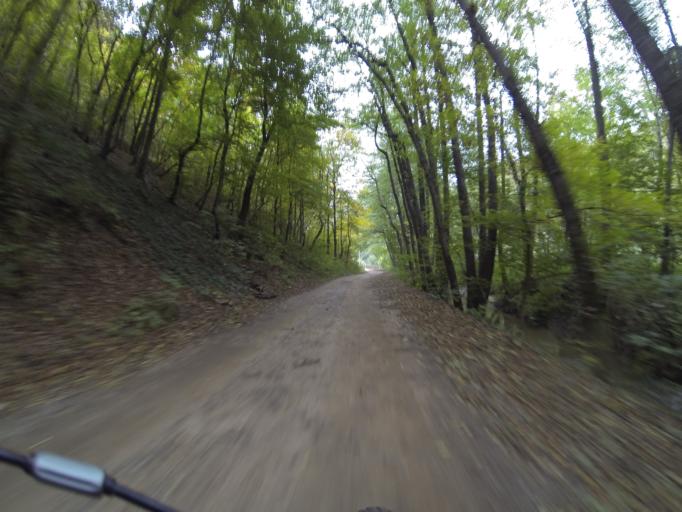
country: RO
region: Gorj
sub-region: Comuna Tismana
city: Pocruia
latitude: 45.0521
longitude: 22.9153
